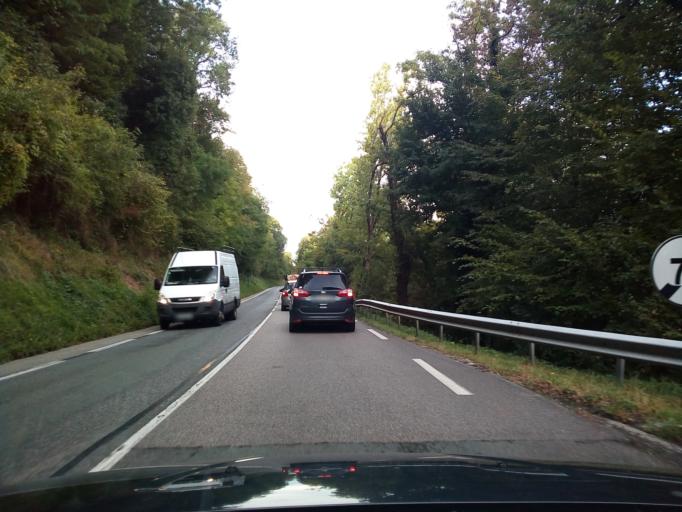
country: FR
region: Rhone-Alpes
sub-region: Departement de l'Isere
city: Goncelin
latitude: 45.3529
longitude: 5.9906
